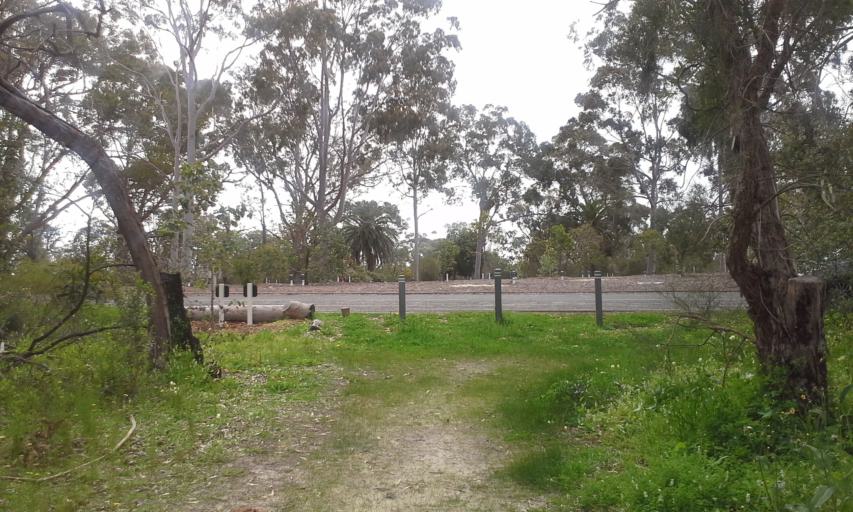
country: AU
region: Western Australia
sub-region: Nedlands
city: Subiaco
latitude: -31.9567
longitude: 115.8330
